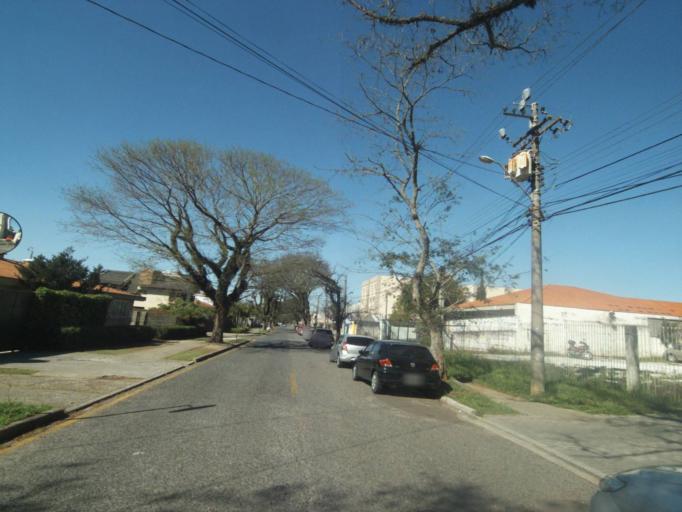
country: BR
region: Parana
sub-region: Curitiba
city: Curitiba
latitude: -25.3981
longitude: -49.2390
